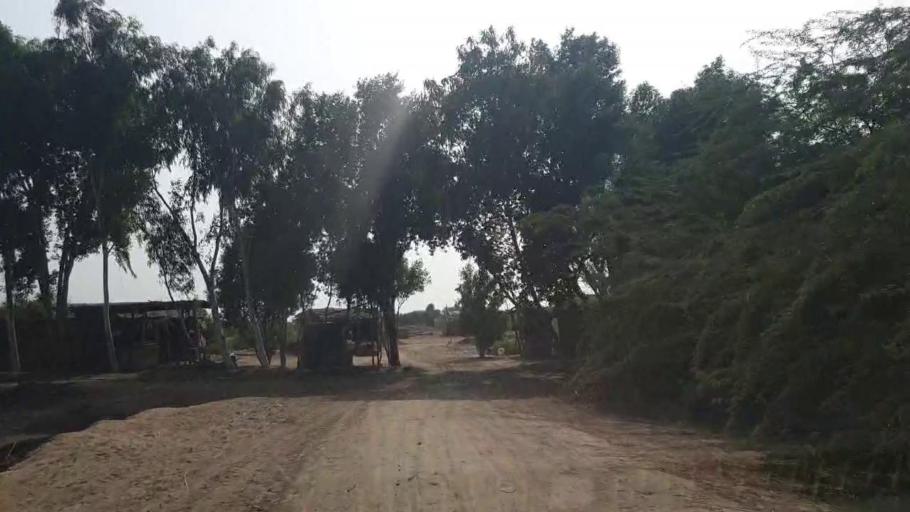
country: PK
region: Sindh
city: Badin
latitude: 24.5418
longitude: 68.6549
